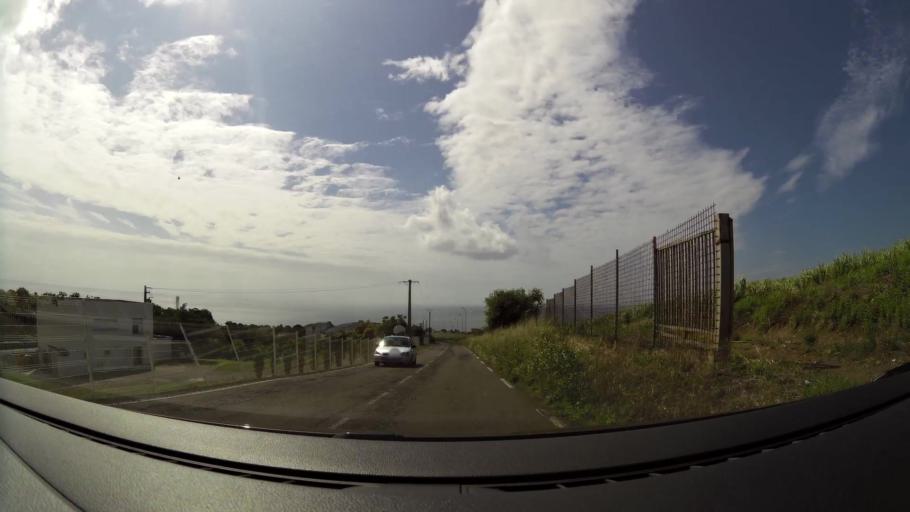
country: GP
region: Guadeloupe
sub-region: Guadeloupe
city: Basse-Terre
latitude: 16.0093
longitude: -61.7282
